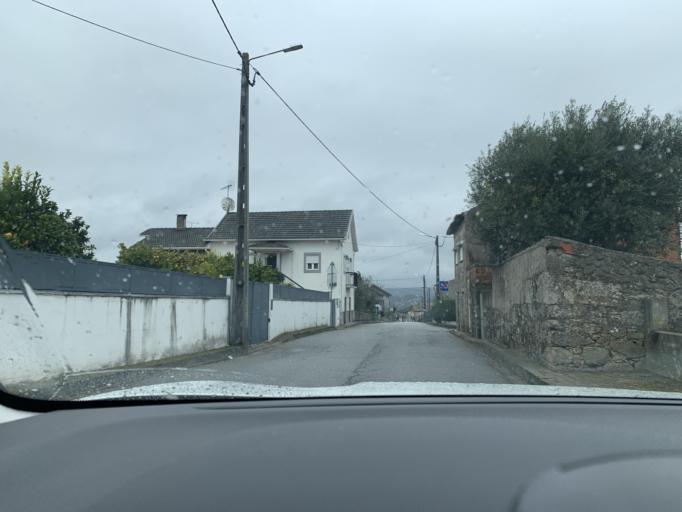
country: PT
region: Viseu
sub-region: Nelas
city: Nelas
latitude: 40.5978
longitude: -7.8435
